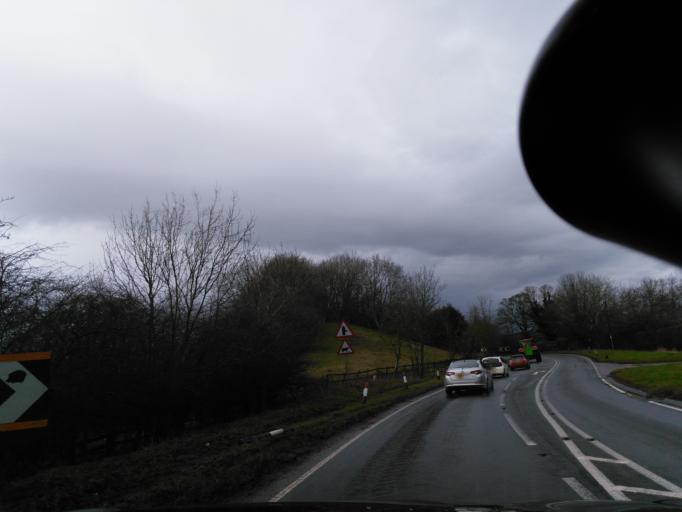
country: GB
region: England
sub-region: North Yorkshire
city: Harrogate
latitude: 54.0622
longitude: -1.5383
